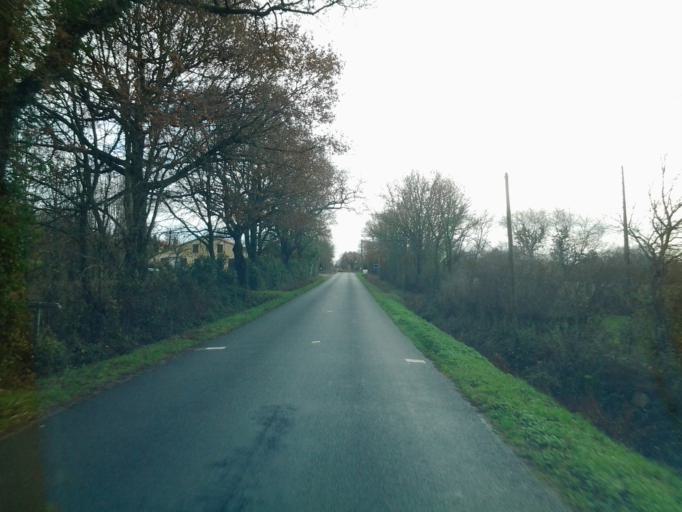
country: FR
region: Pays de la Loire
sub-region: Departement de la Vendee
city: Nesmy
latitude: 46.6410
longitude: -1.3613
